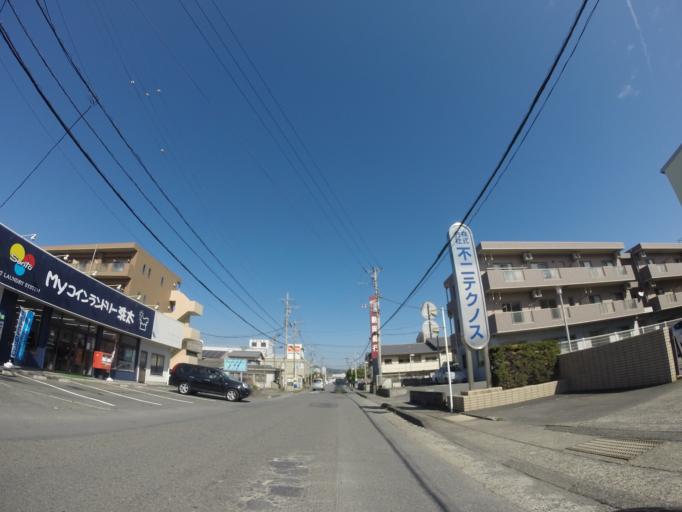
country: JP
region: Shizuoka
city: Numazu
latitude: 35.1151
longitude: 138.8314
